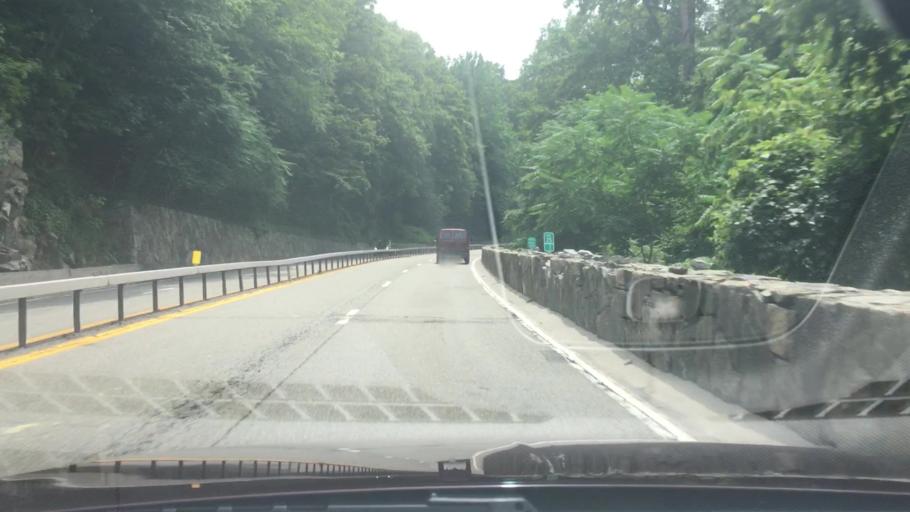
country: US
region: New York
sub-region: Putnam County
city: Mahopac
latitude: 41.3990
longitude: -73.7922
